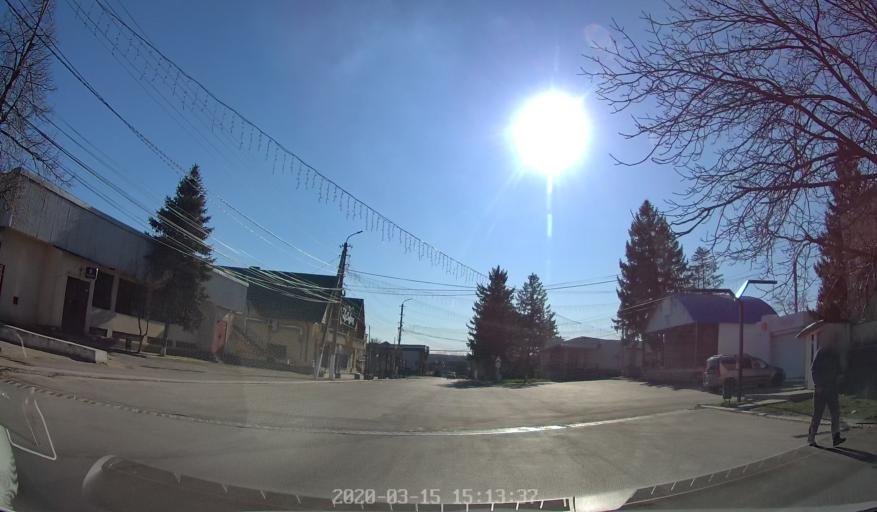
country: MD
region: Chisinau
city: Cricova
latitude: 47.2495
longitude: 28.7701
